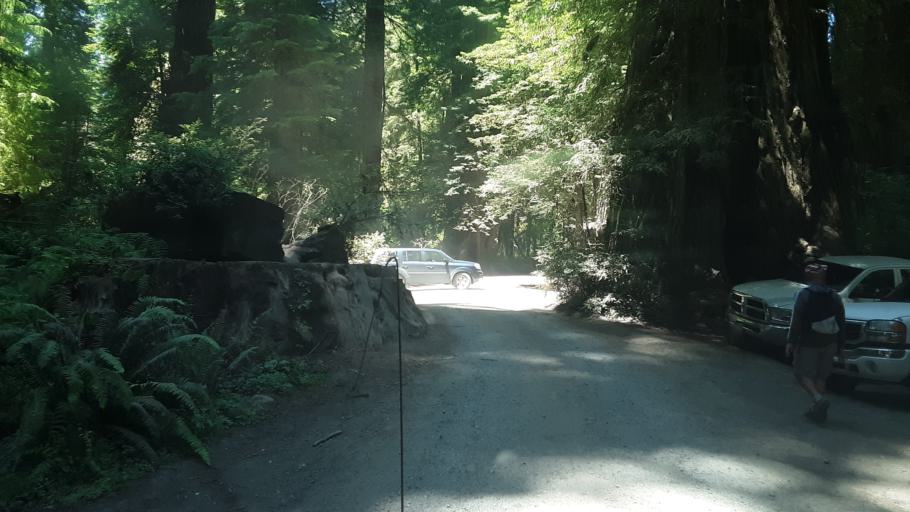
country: US
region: California
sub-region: Del Norte County
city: Bertsch-Oceanview
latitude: 41.8131
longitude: -124.1099
